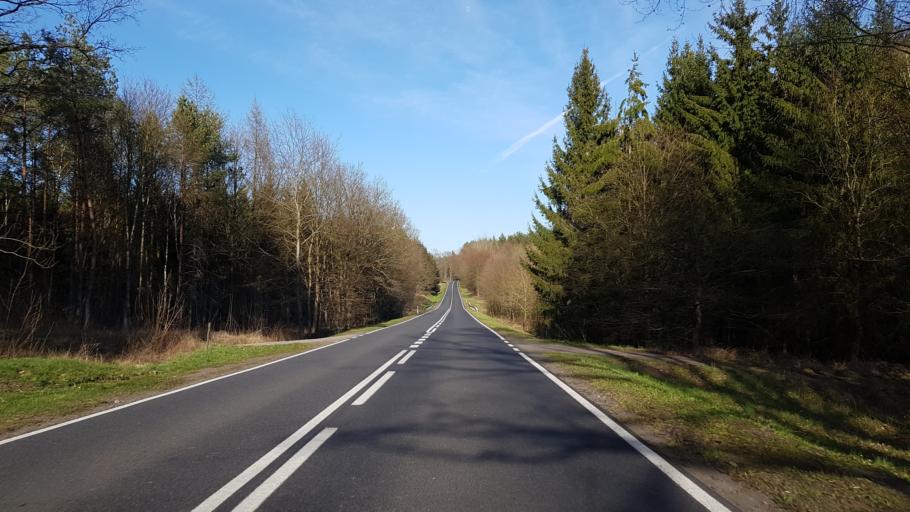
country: PL
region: West Pomeranian Voivodeship
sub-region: Powiat stargardzki
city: Chociwel
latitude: 53.4845
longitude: 15.3974
